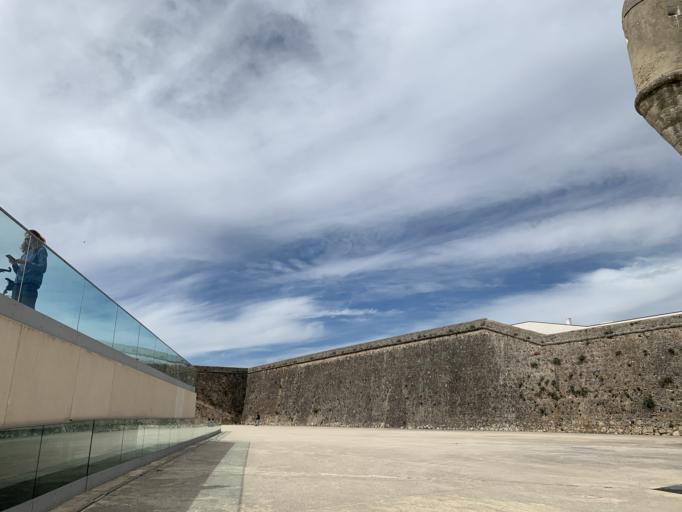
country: PT
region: Lisbon
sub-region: Cascais
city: Cascais
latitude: 38.6933
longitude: -9.4204
